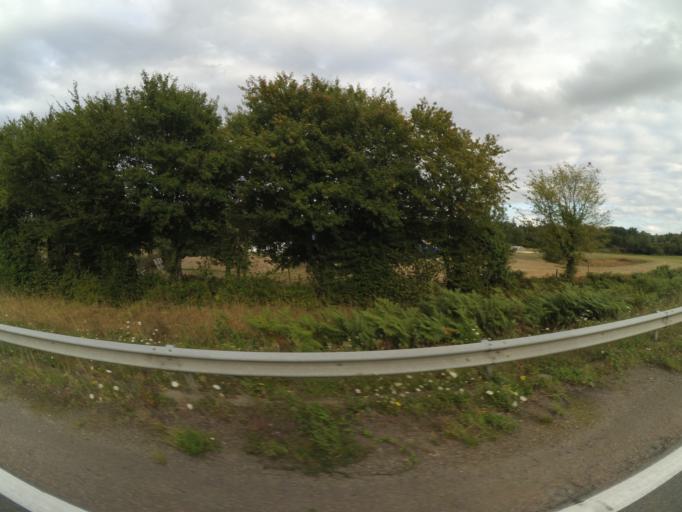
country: FR
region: Pays de la Loire
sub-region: Departement de la Vendee
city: Saligny
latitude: 46.8387
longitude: -1.4197
